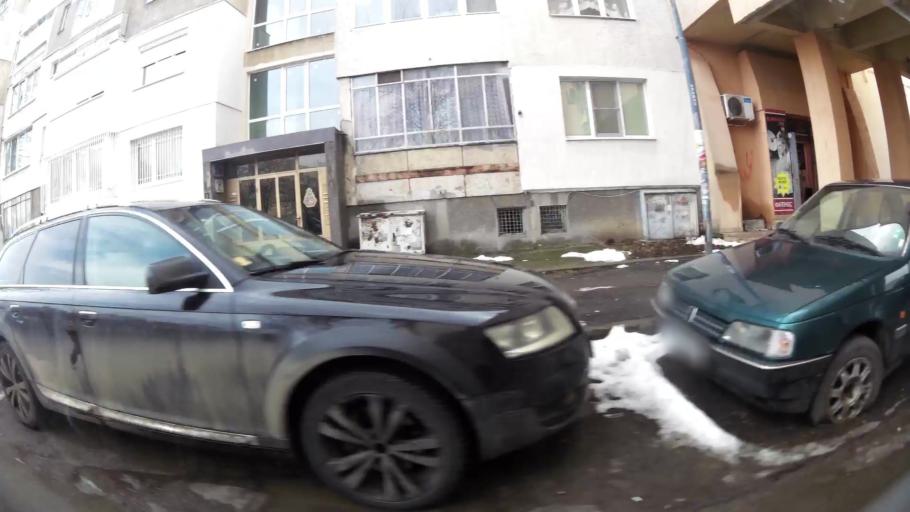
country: BG
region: Sofiya
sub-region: Obshtina Bozhurishte
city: Bozhurishte
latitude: 42.7185
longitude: 23.2481
